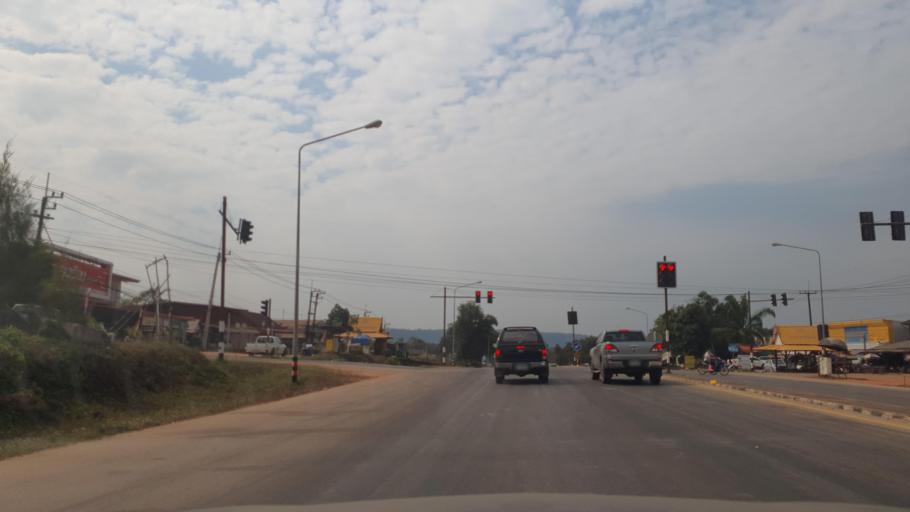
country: TH
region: Changwat Bueng Kan
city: Bung Khla
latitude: 18.2761
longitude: 103.8563
